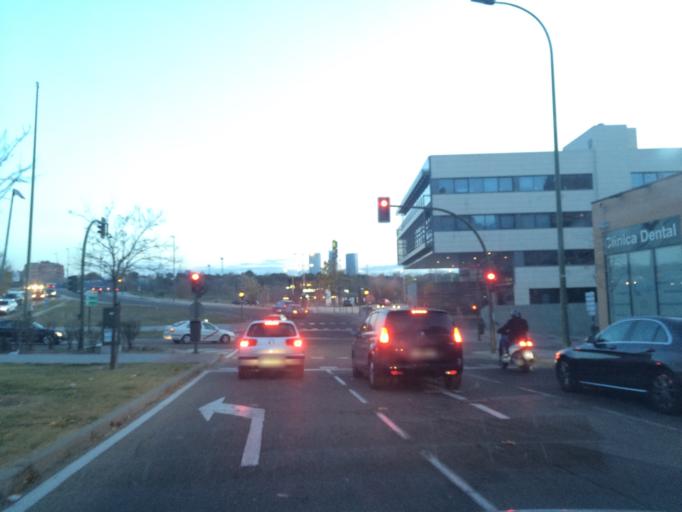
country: ES
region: Madrid
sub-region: Provincia de Madrid
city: Las Tablas
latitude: 40.5029
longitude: -3.6980
